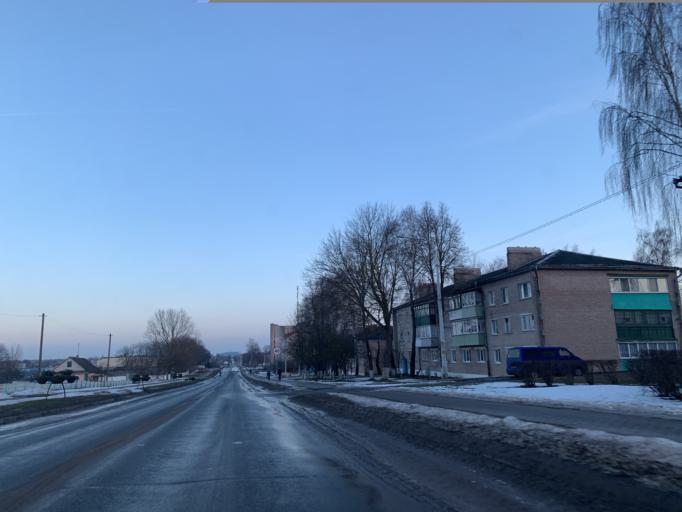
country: BY
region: Minsk
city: Nyasvizh
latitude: 53.2317
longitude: 26.6549
